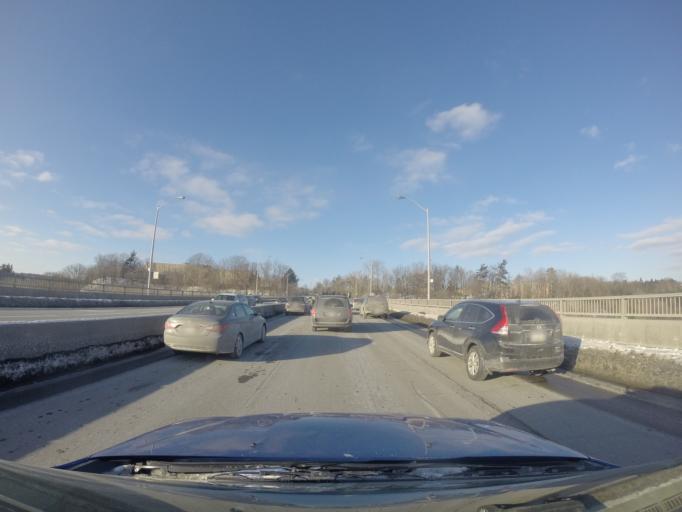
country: CA
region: Ontario
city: Willowdale
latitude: 43.7303
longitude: -79.3813
